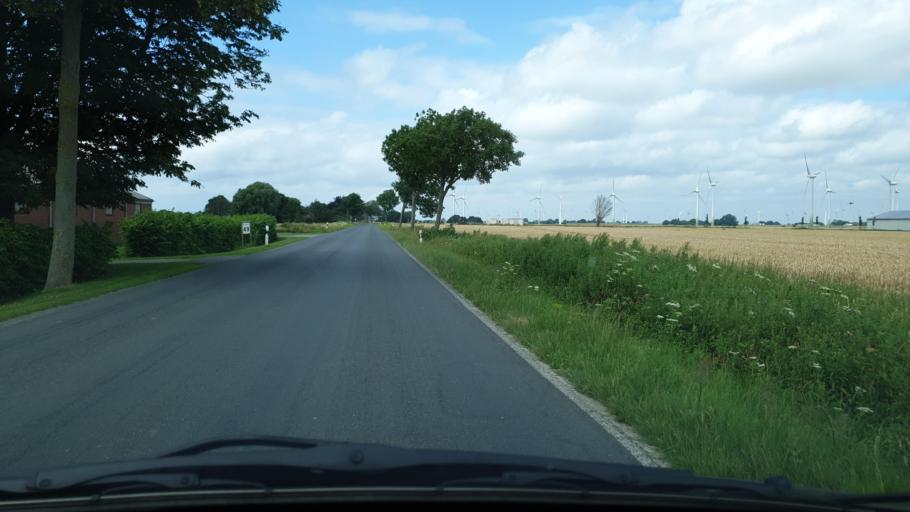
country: DE
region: Schleswig-Holstein
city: Kronprinzenkoog
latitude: 53.9670
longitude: 8.9284
